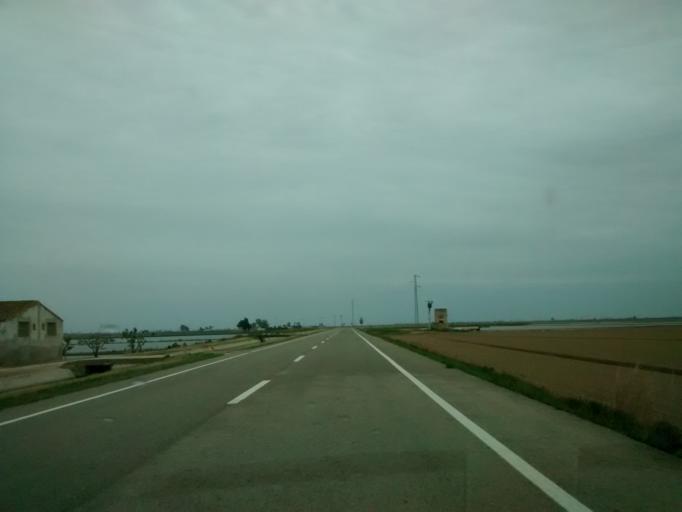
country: ES
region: Catalonia
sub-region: Provincia de Tarragona
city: Deltebre
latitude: 40.6961
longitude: 0.6802
